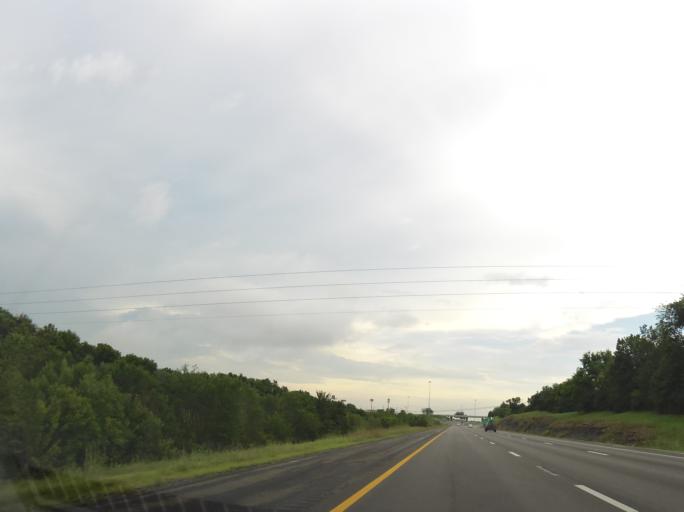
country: US
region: Kentucky
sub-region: Madison County
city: Richmond
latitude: 37.7279
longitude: -84.3225
